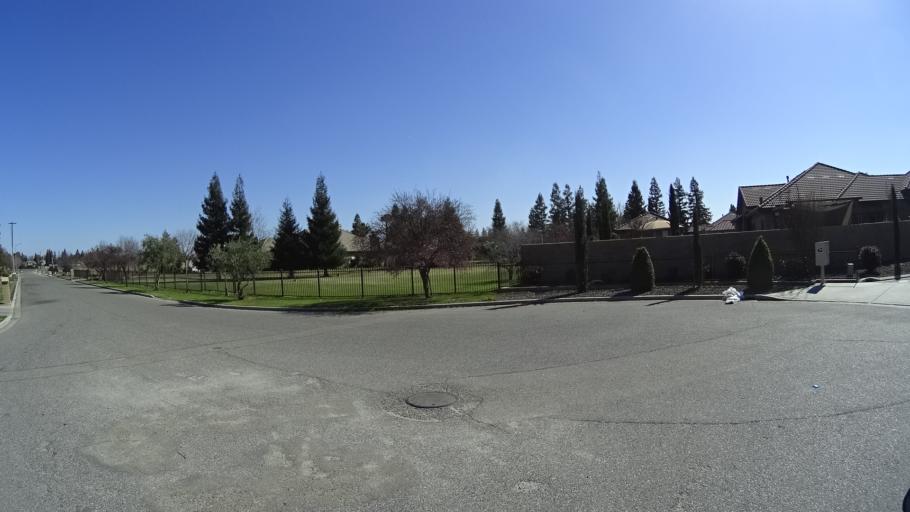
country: US
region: California
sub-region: Fresno County
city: Clovis
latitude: 36.8623
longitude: -119.7513
